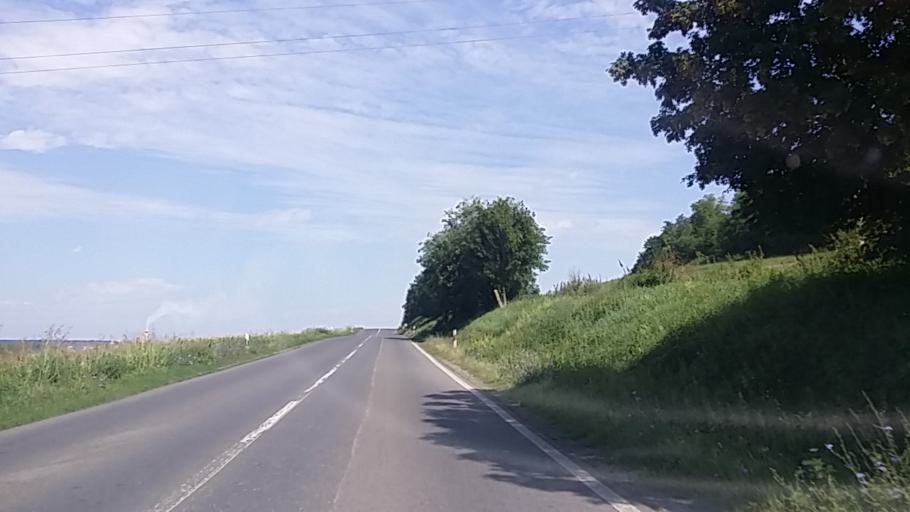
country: HU
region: Baranya
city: Sasd
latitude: 46.2339
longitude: 18.1212
